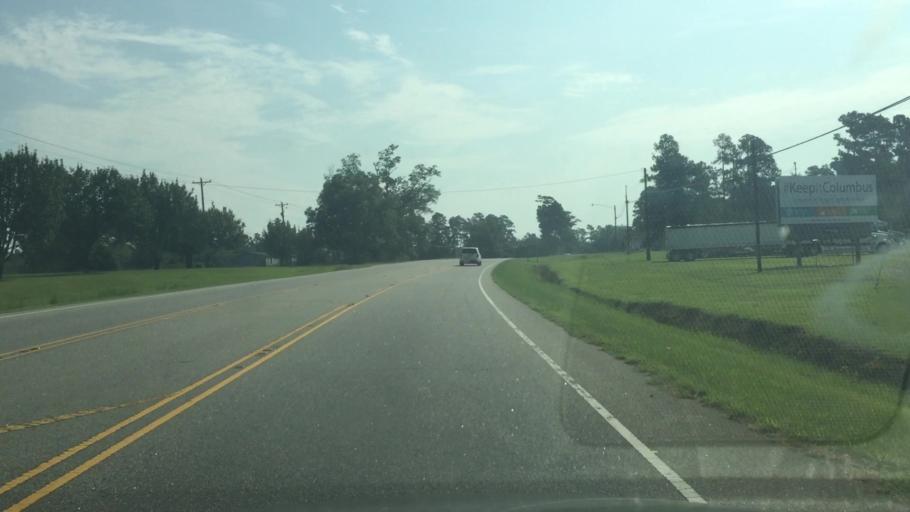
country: US
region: North Carolina
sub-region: Columbus County
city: Tabor City
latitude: 34.1580
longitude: -78.8557
